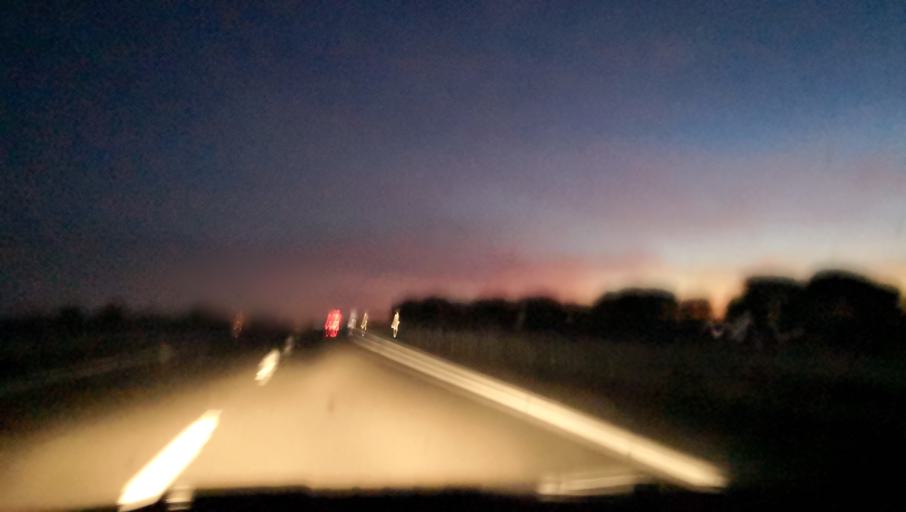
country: PT
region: Santarem
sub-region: Benavente
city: Poceirao
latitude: 38.7692
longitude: -8.6829
